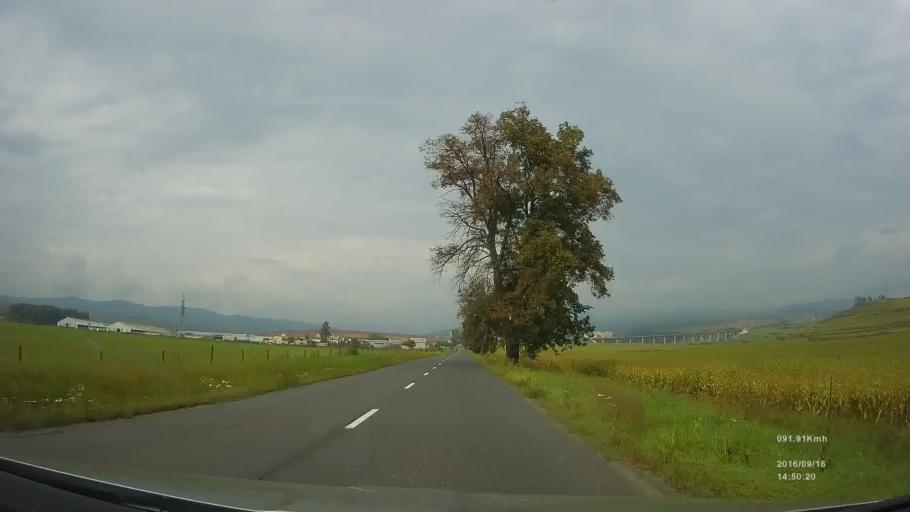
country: SK
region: Presovsky
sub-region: Okres Presov
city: Levoca
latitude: 48.9954
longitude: 20.5821
